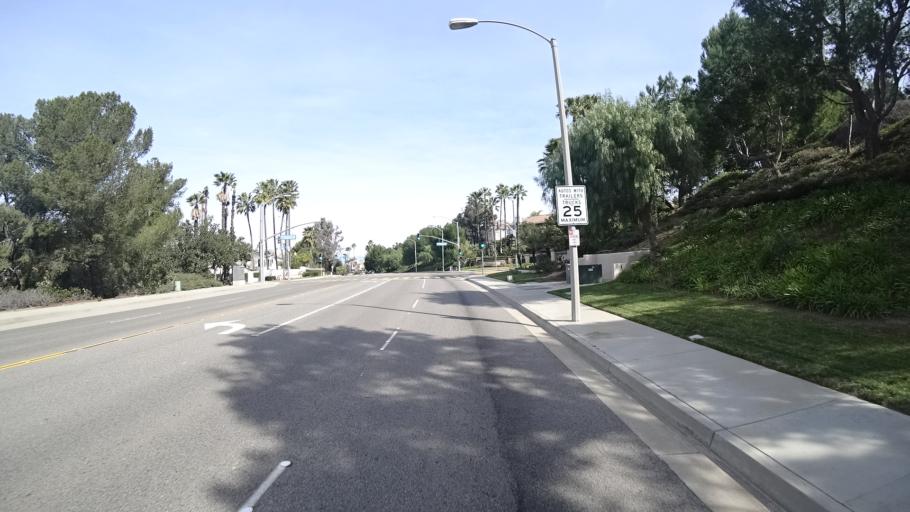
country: US
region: California
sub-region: Orange County
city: Villa Park
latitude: 33.8452
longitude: -117.7392
